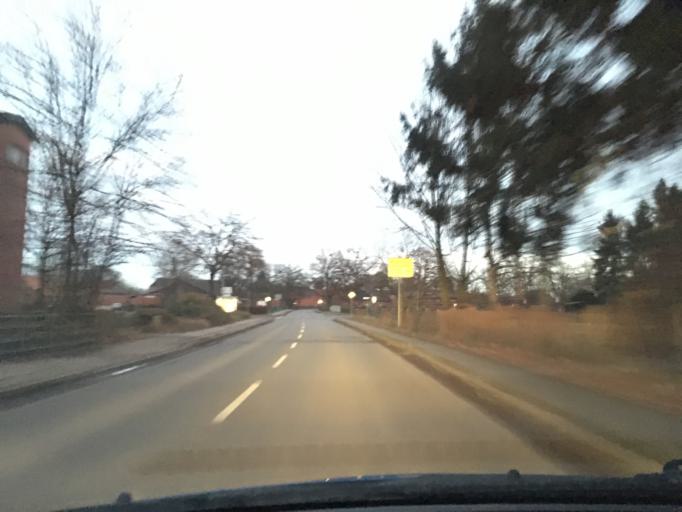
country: DE
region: Lower Saxony
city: Barum
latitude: 53.3515
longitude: 10.4075
